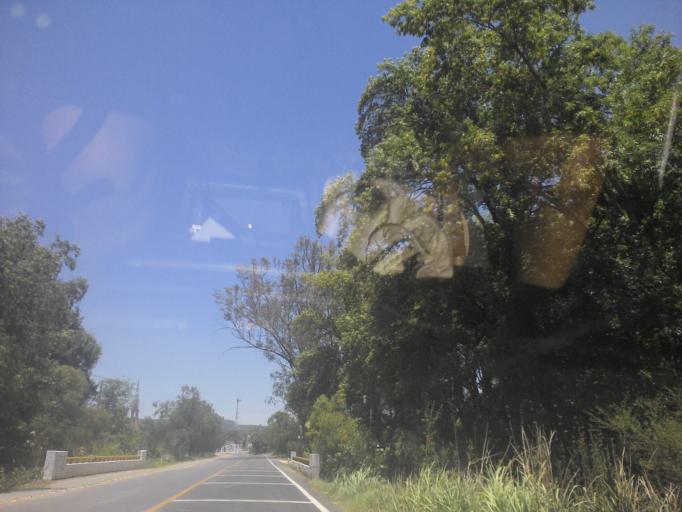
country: MX
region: Jalisco
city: San Diego de Alejandria
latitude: 20.8763
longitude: -101.9830
